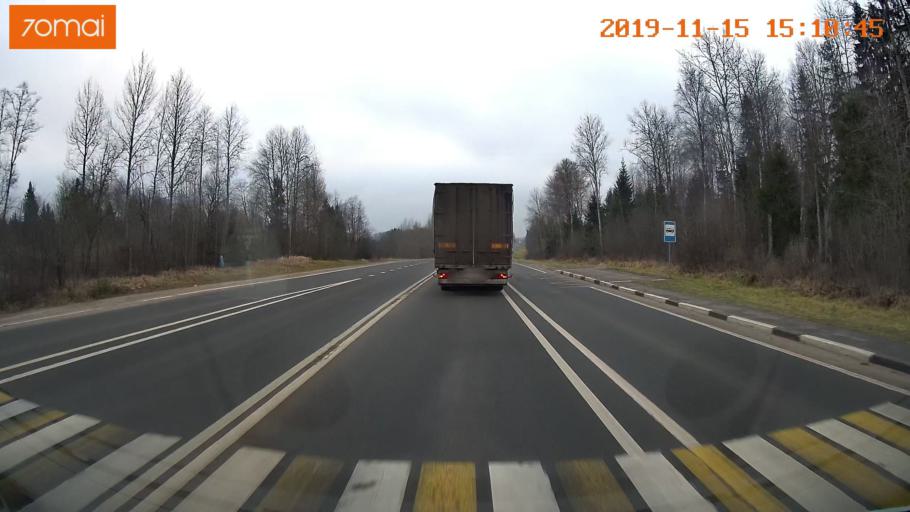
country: RU
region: Jaroslavl
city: Prechistoye
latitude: 58.3445
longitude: 40.2510
